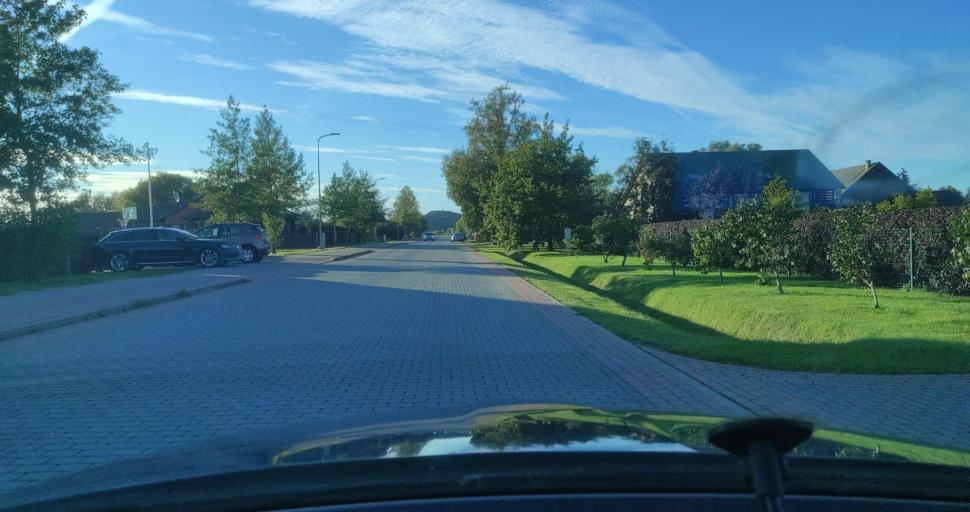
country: LV
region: Ventspils
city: Ventspils
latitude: 57.3664
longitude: 21.5700
